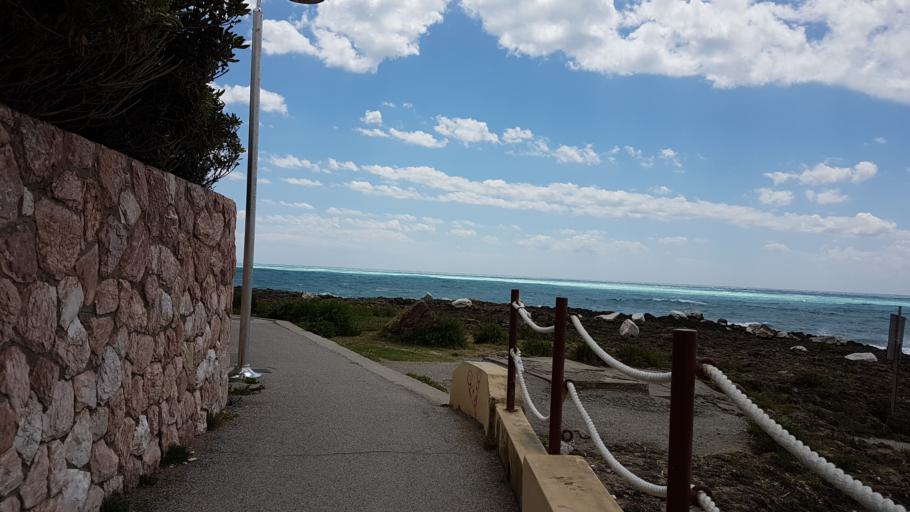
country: IT
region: Tuscany
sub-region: Provincia di Livorno
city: Rosignano Solvay-Castiglioncello
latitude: 43.4011
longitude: 10.4216
